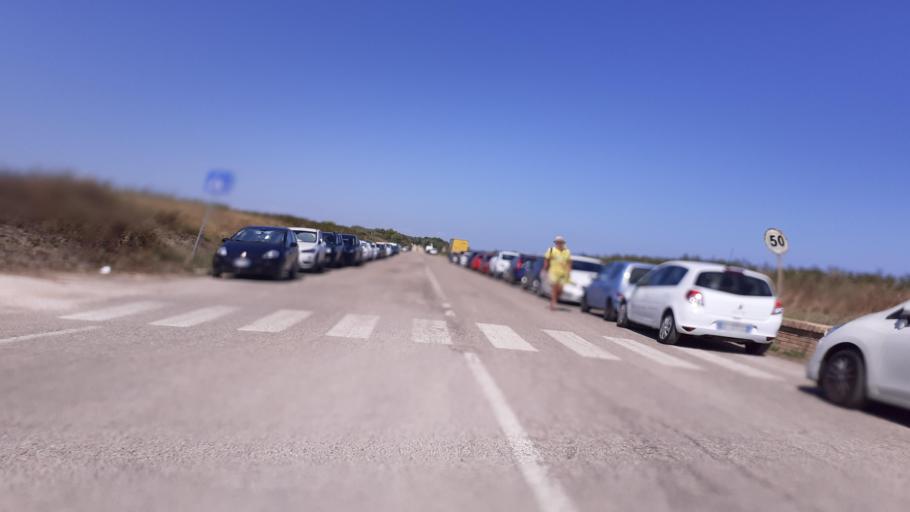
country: IT
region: Abruzzo
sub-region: Provincia di Chieti
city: Vasto
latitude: 42.1727
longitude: 14.7012
